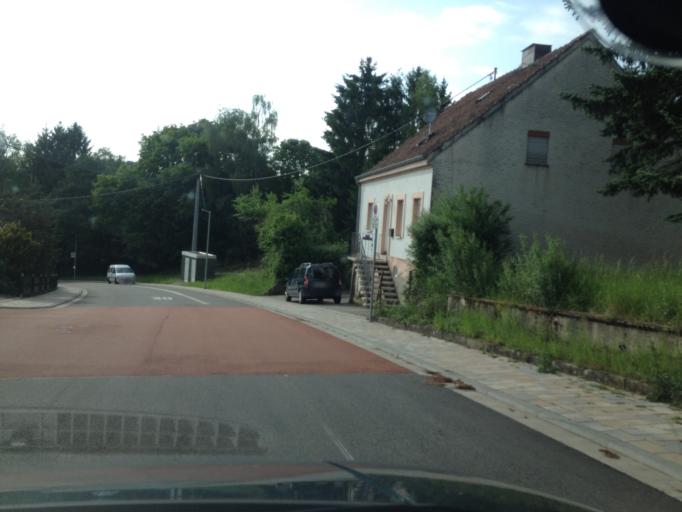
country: DE
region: Saarland
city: Schiffweiler
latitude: 49.3728
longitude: 7.1168
